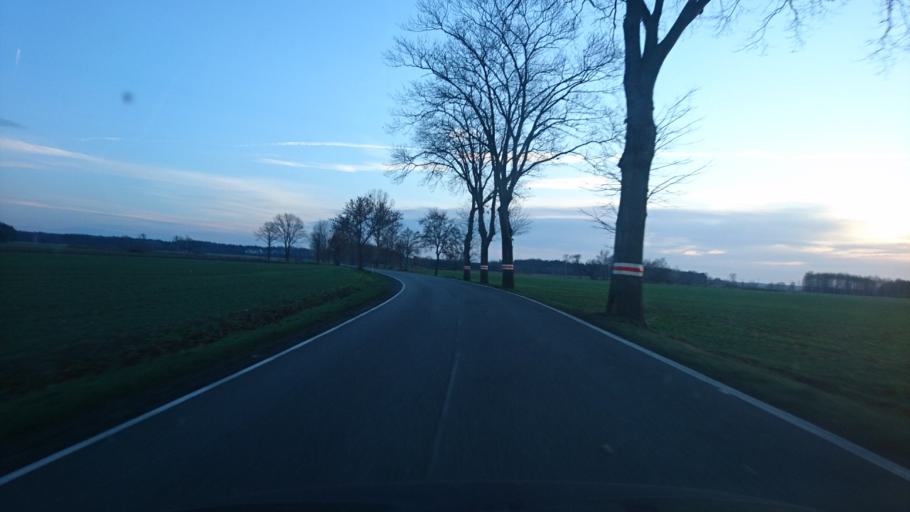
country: PL
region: Greater Poland Voivodeship
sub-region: Powiat ostrowski
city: Odolanow
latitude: 51.5628
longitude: 17.6966
